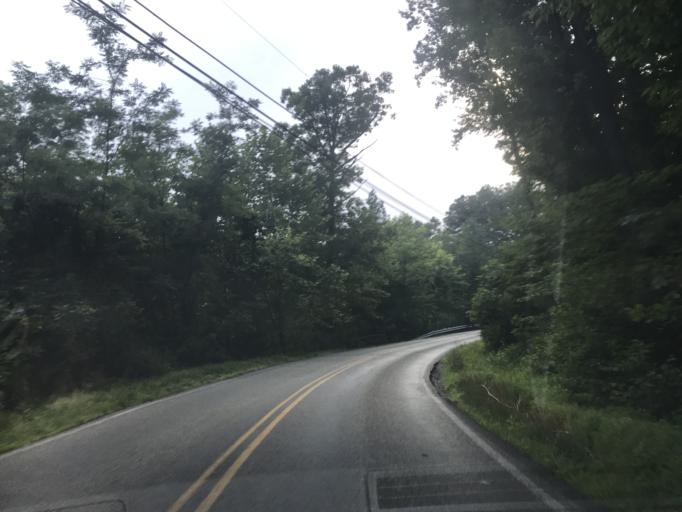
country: US
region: Maryland
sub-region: Harford County
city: Bel Air South
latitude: 39.5025
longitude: -76.3048
